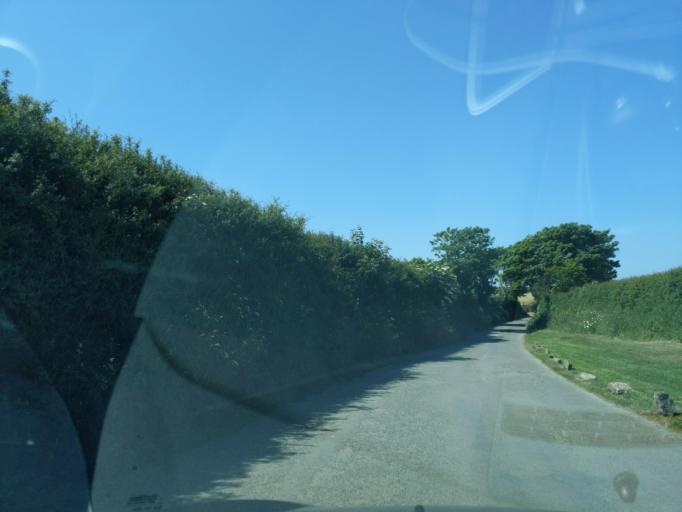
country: GB
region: England
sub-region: Cornwall
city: Wadebridge
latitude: 50.5760
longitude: -4.8300
